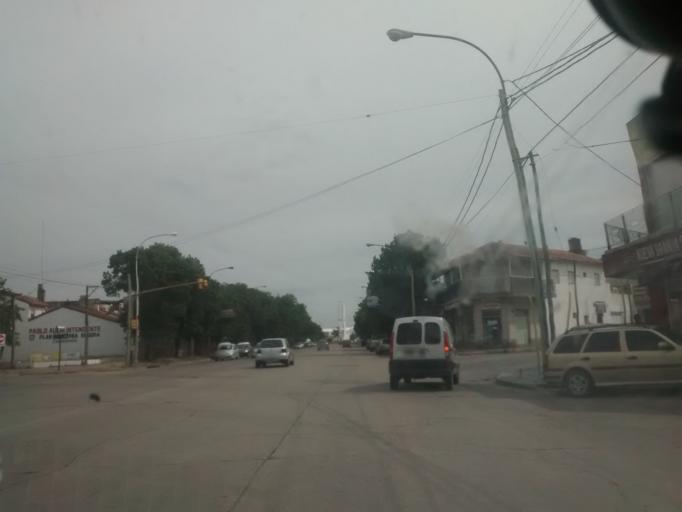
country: AR
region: Buenos Aires
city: Necochea
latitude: -38.5653
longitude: -58.7295
